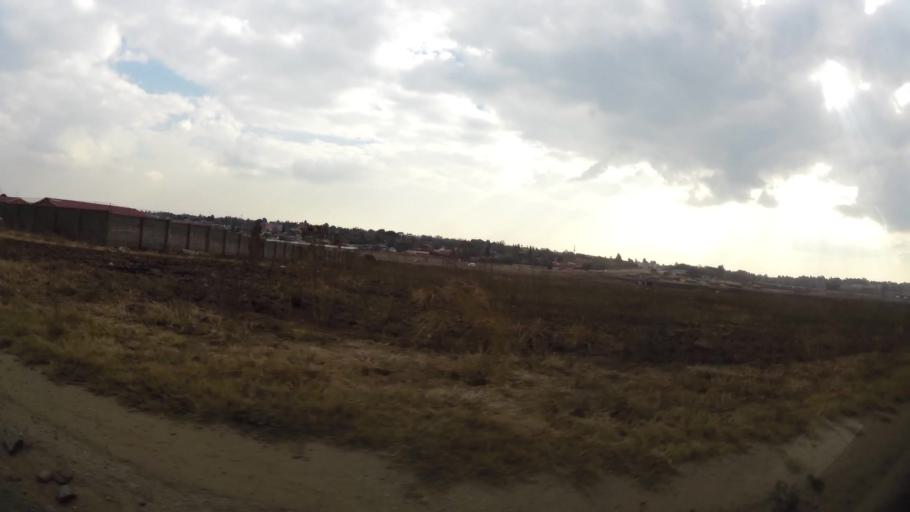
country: ZA
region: Gauteng
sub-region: Ekurhuleni Metropolitan Municipality
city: Benoni
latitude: -26.1389
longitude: 28.3568
